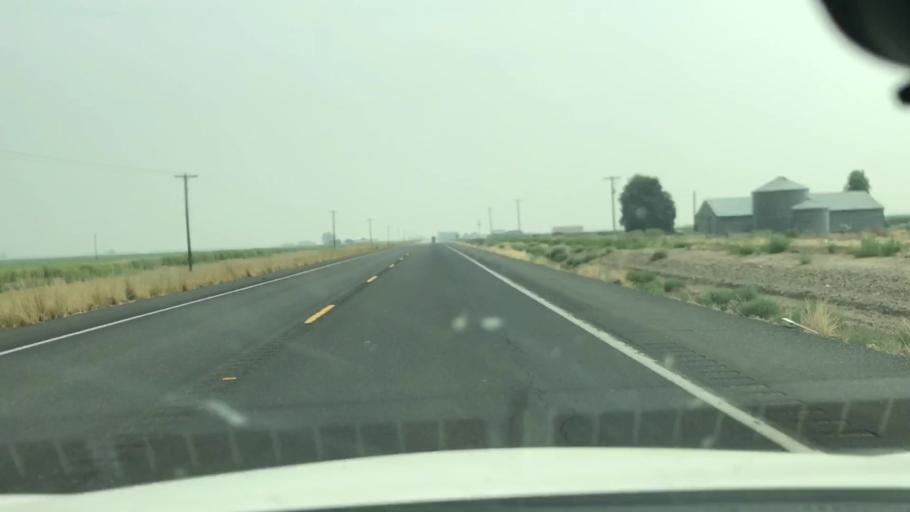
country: US
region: Washington
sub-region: Grant County
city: Quincy
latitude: 47.2341
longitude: -119.7989
